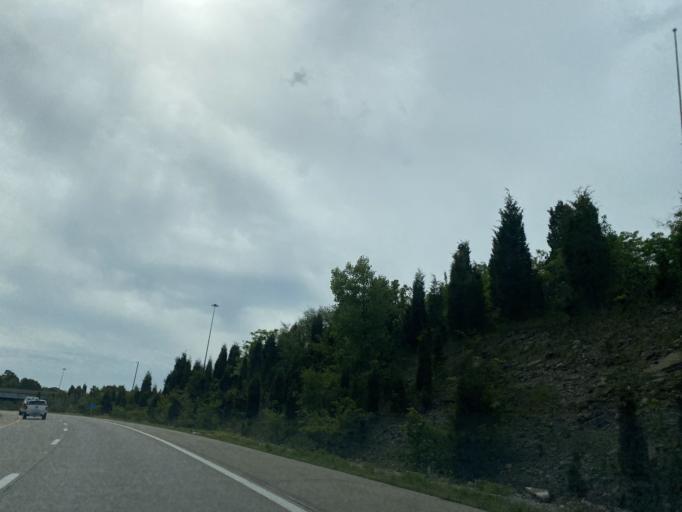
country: US
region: Kentucky
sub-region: Campbell County
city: Highland Heights
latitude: 39.0467
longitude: -84.4607
